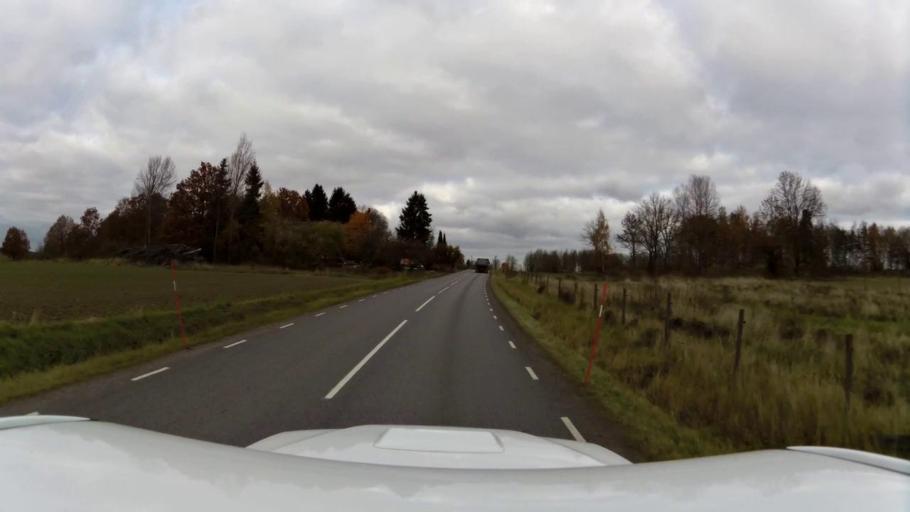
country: SE
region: OEstergoetland
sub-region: Linkopings Kommun
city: Linghem
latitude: 58.4051
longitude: 15.7647
